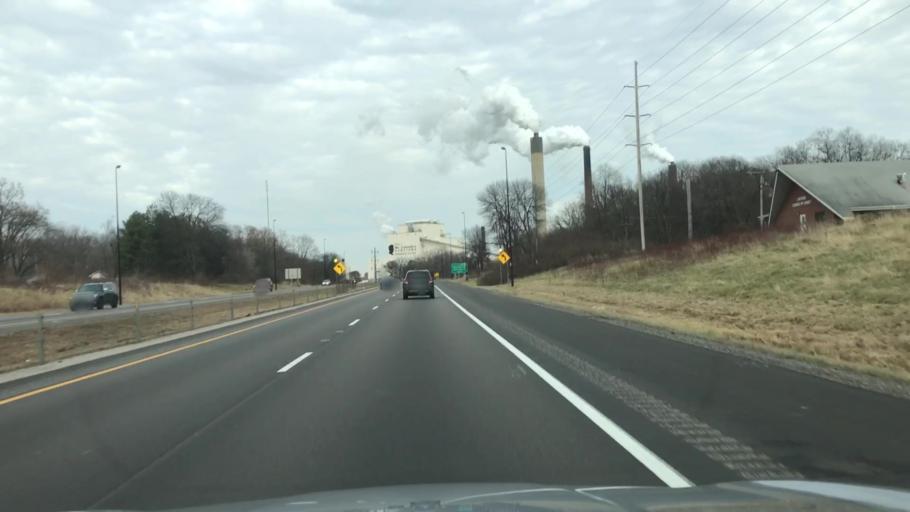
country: US
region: Illinois
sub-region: Sangamon County
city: Southern View
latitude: 39.7510
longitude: -89.6140
